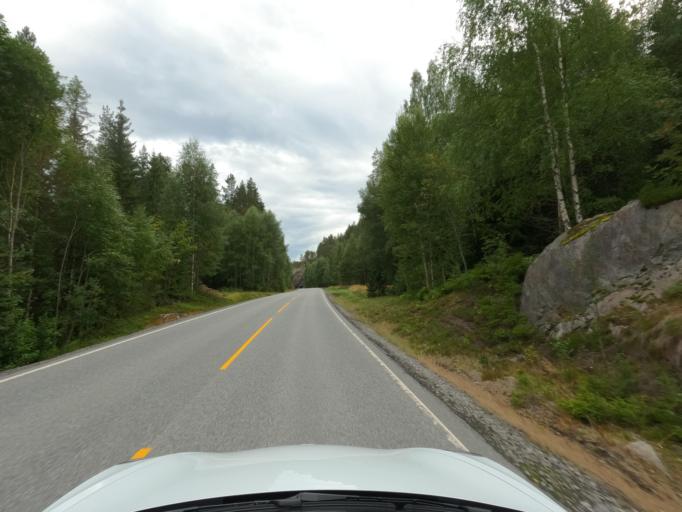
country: NO
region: Telemark
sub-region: Hjartdal
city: Sauland
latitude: 59.7394
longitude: 9.0204
